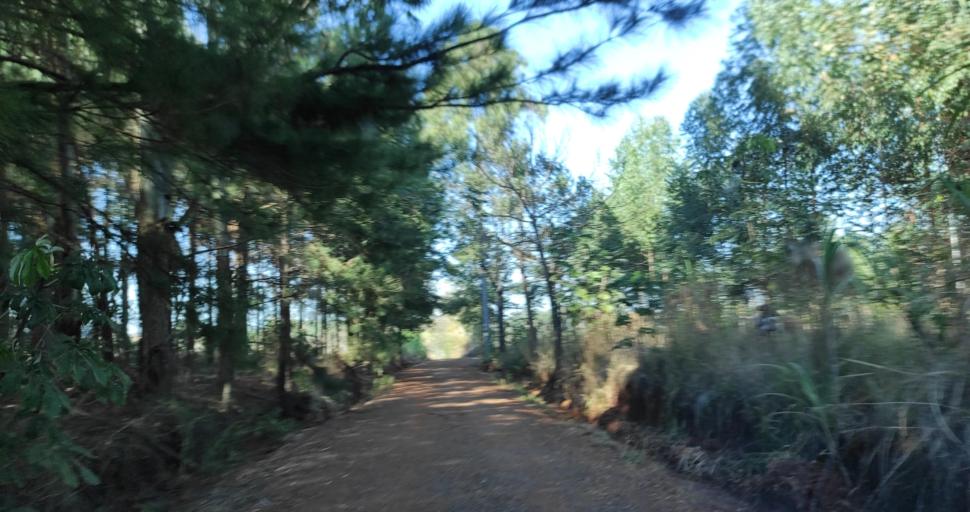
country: AR
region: Misiones
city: Capiovi
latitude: -26.8931
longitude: -55.0383
